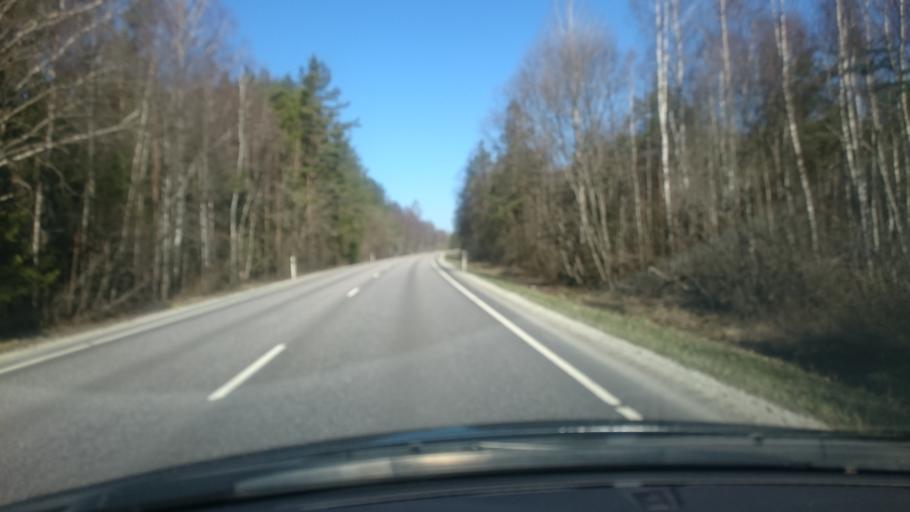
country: EE
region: Raplamaa
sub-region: Kehtna vald
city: Kehtna
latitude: 58.8654
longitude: 24.9903
